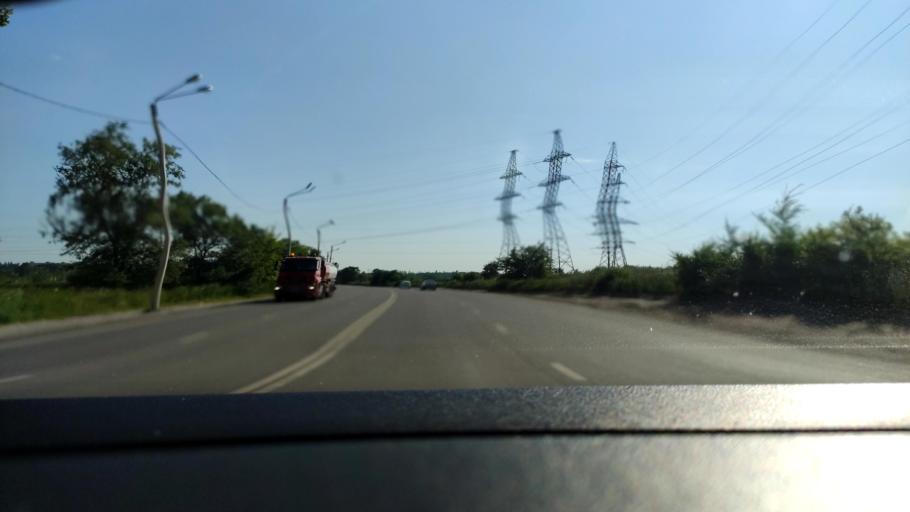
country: RU
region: Voronezj
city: Maslovka
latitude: 51.6205
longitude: 39.2743
